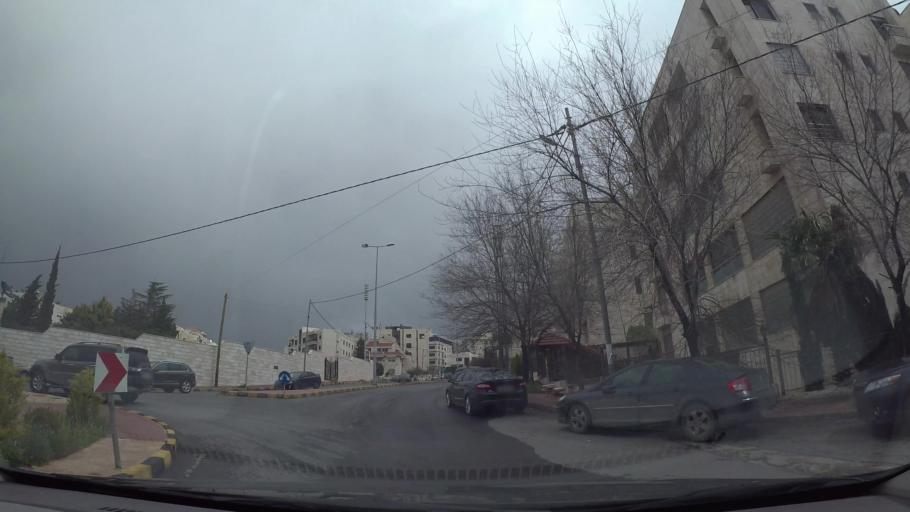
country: JO
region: Amman
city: Wadi as Sir
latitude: 31.9428
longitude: 35.8590
